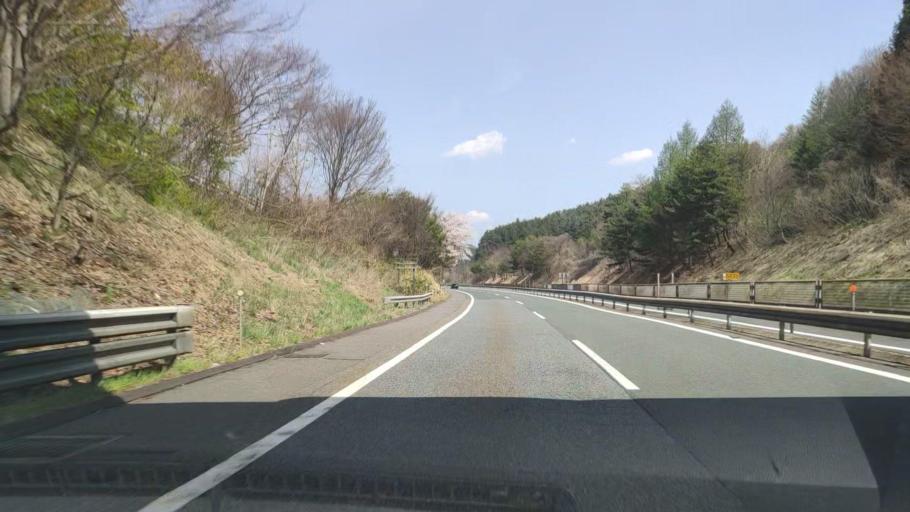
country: JP
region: Iwate
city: Ichinohe
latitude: 40.1868
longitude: 141.1720
